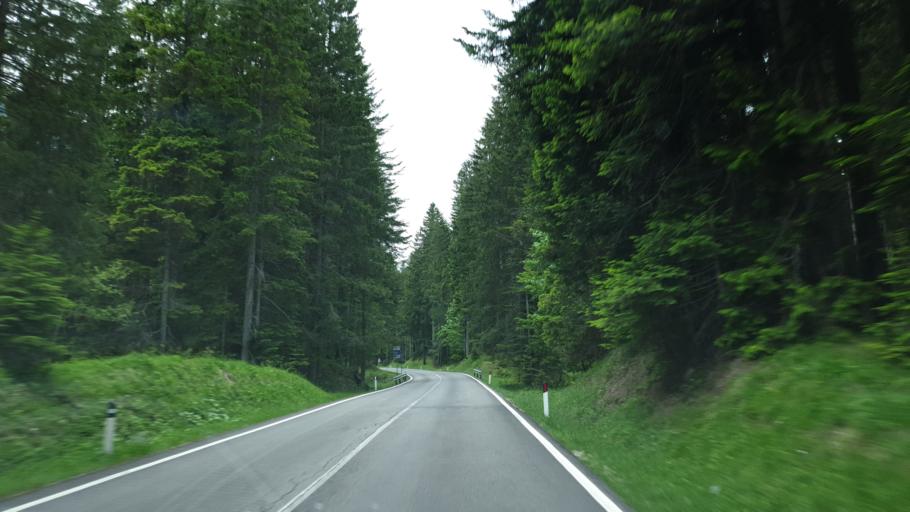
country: IT
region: Veneto
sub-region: Provincia di Belluno
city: San Vito
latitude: 46.5317
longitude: 12.2777
